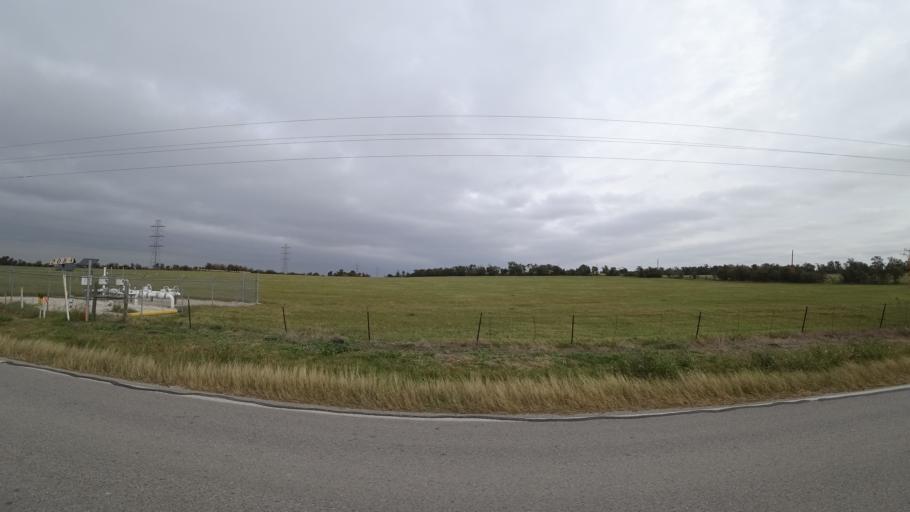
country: US
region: Texas
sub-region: Travis County
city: Pflugerville
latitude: 30.4109
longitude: -97.5632
